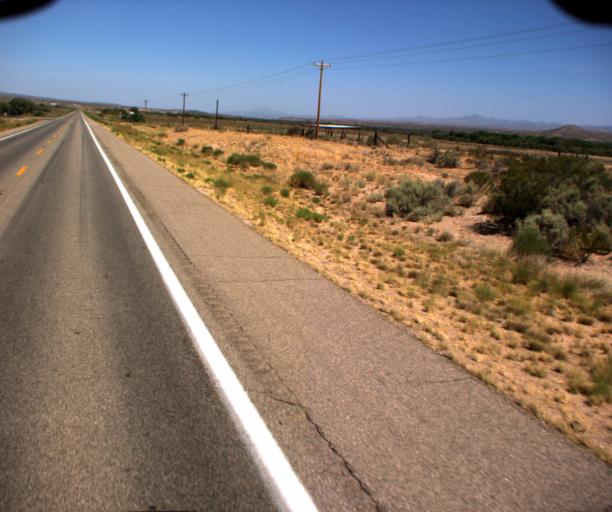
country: US
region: Arizona
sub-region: Graham County
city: Bylas
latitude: 33.0831
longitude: -110.0488
